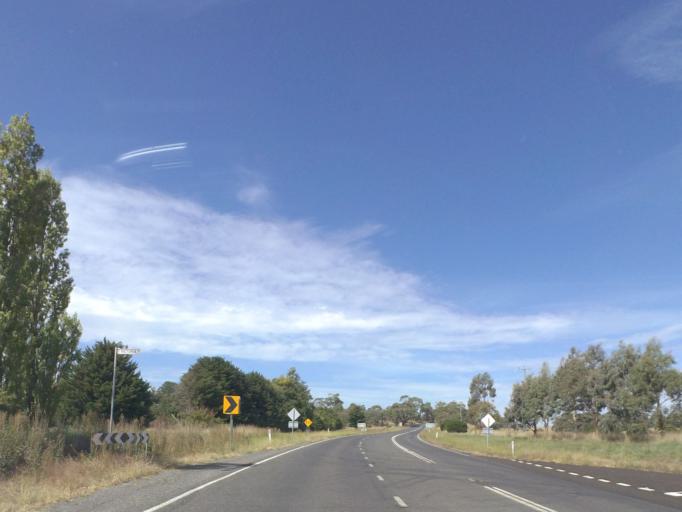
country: AU
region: Victoria
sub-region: Mount Alexander
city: Castlemaine
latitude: -37.2709
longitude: 144.4801
